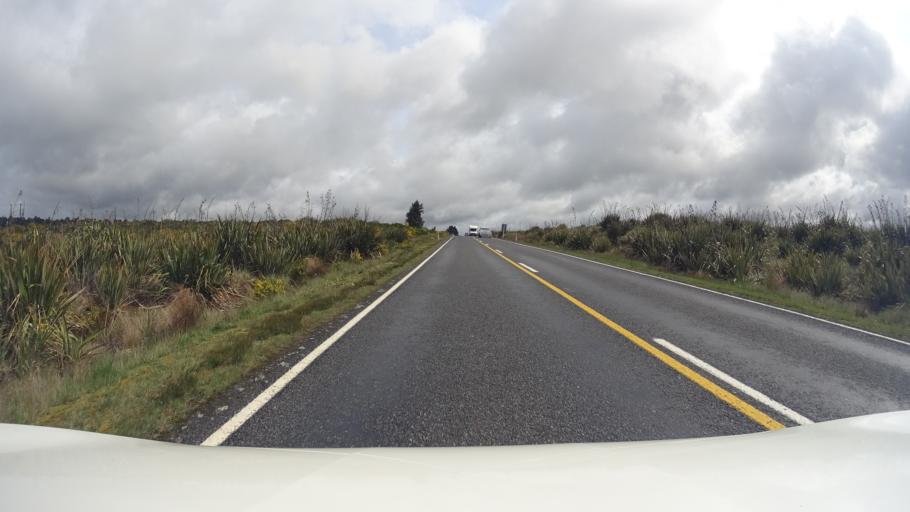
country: NZ
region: Manawatu-Wanganui
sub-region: Ruapehu District
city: Waiouru
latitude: -39.1884
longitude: 175.4018
